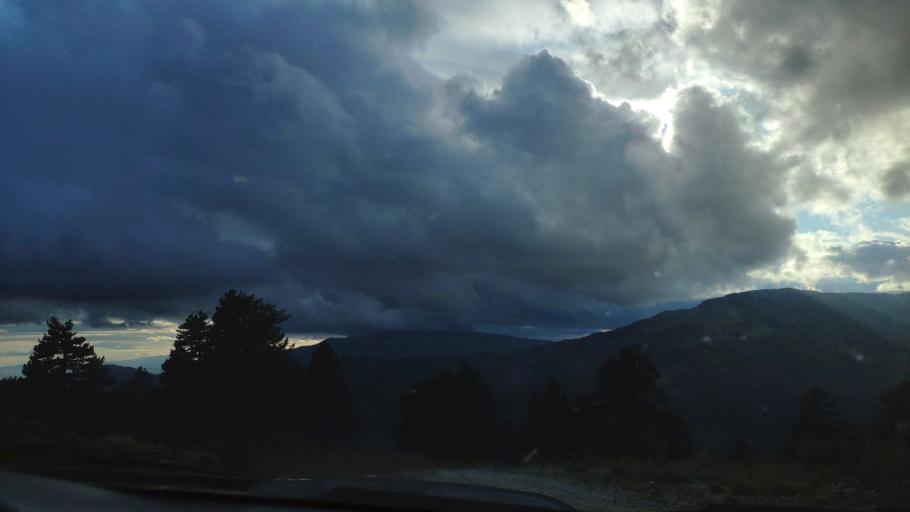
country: AL
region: Korce
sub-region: Rrethi i Kolonjes
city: Erseke
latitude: 40.2915
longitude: 20.8774
